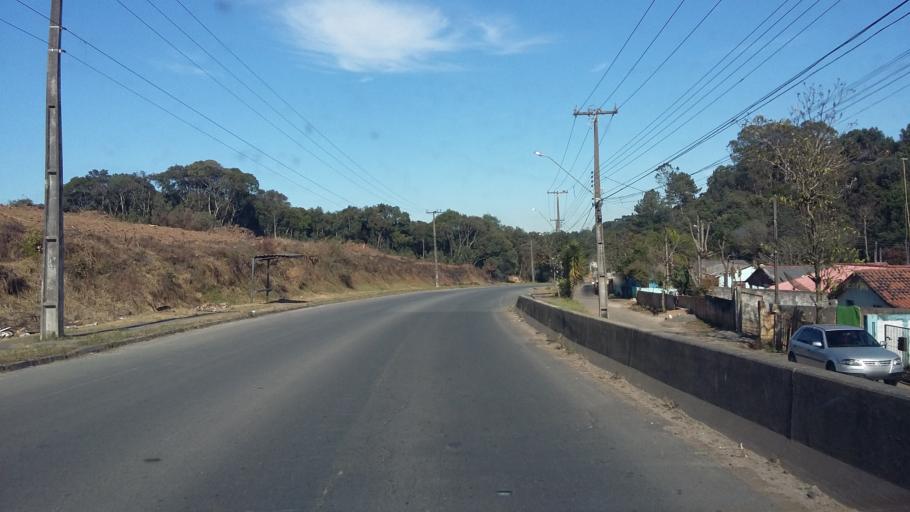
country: BR
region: Parana
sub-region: Campo Largo
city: Campo Largo
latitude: -25.4587
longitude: -49.5565
